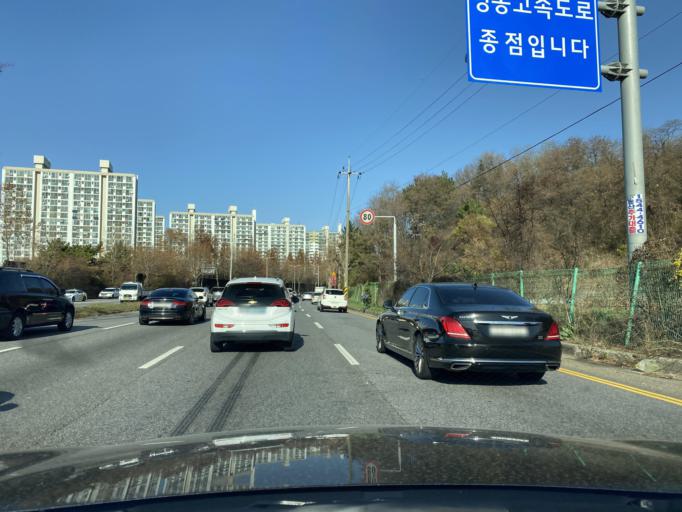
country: KR
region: Incheon
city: Incheon
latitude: 37.4378
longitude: 126.7398
